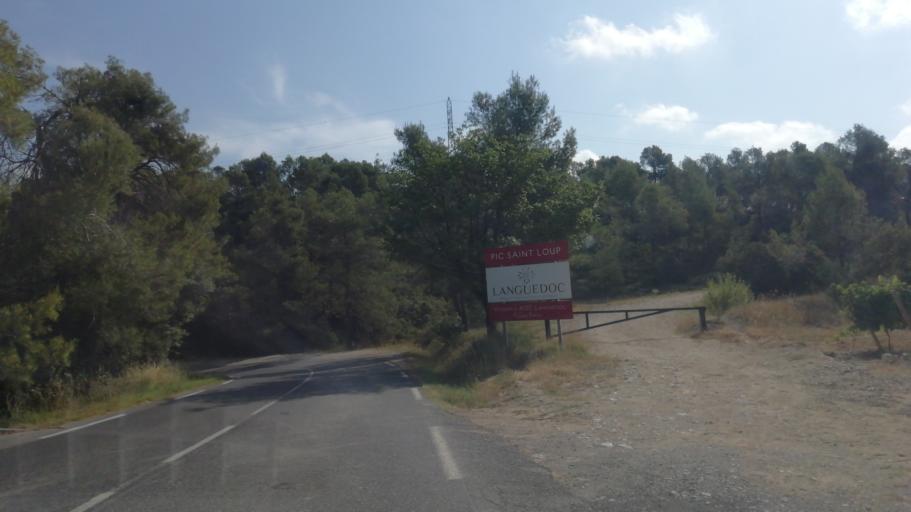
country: FR
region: Languedoc-Roussillon
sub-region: Departement de l'Herault
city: Les Matelles
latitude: 43.7259
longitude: 3.8011
